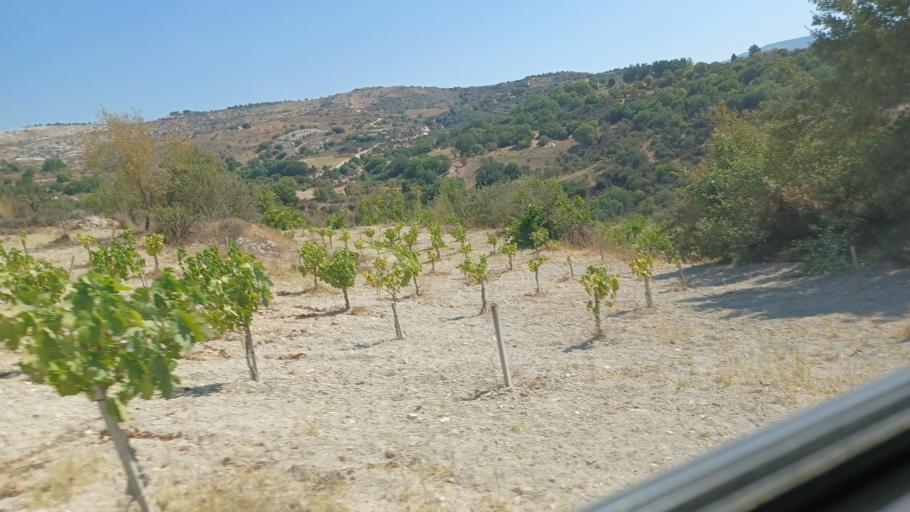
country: CY
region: Pafos
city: Mesogi
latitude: 34.8850
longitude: 32.5306
